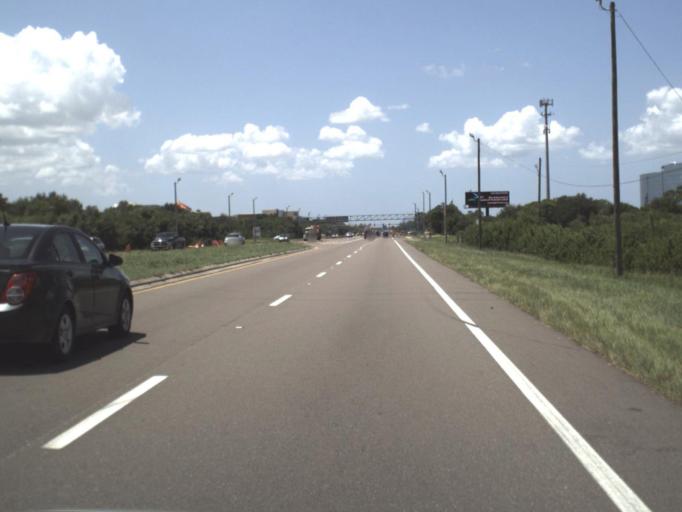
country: US
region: Florida
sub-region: Pinellas County
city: Feather Sound
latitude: 27.8939
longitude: -82.6568
